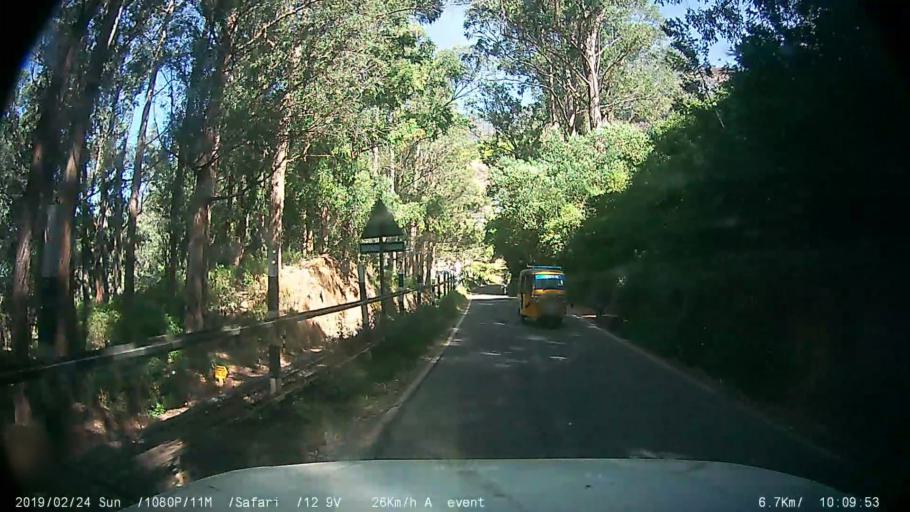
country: IN
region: Tamil Nadu
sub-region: Nilgiri
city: Aravankadu
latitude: 11.3802
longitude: 76.7386
